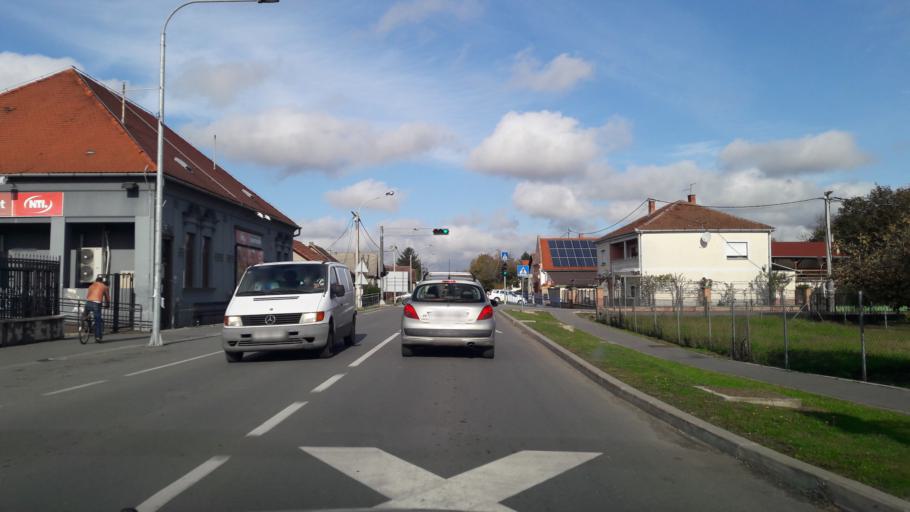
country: HR
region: Osjecko-Baranjska
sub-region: Grad Osijek
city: Bilje
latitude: 45.6050
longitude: 18.7433
